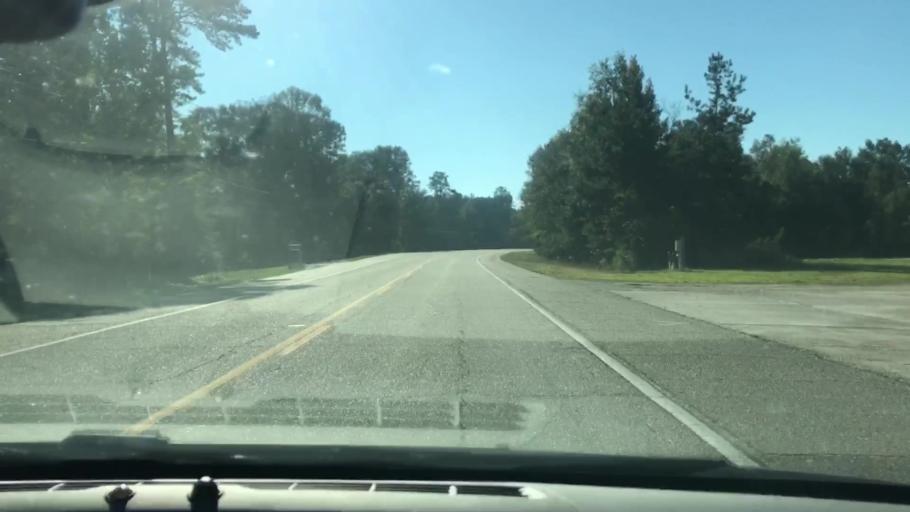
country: US
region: Mississippi
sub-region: Pearl River County
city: Nicholson
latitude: 30.5020
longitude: -89.8155
